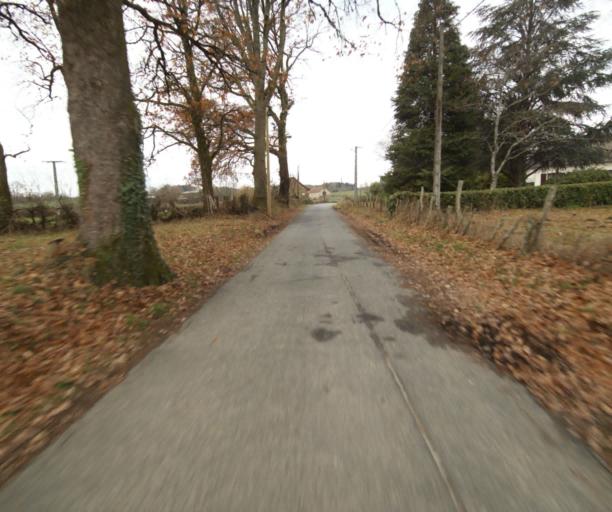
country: FR
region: Limousin
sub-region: Departement de la Correze
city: Chameyrat
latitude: 45.2416
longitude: 1.7177
